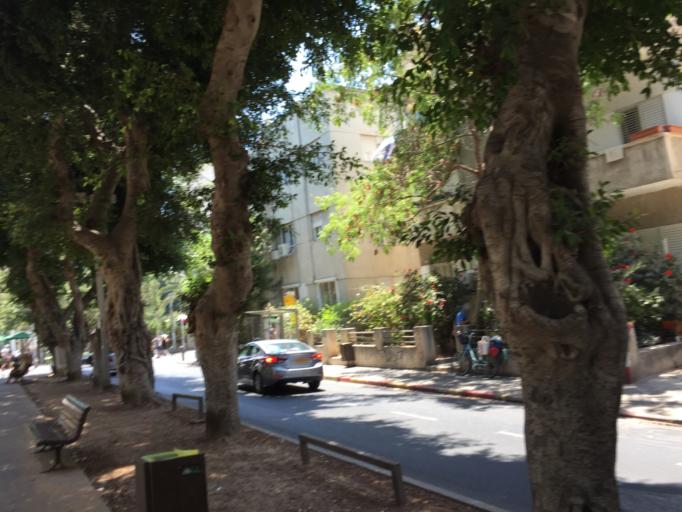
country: IL
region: Tel Aviv
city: Tel Aviv
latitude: 32.0663
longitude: 34.7775
